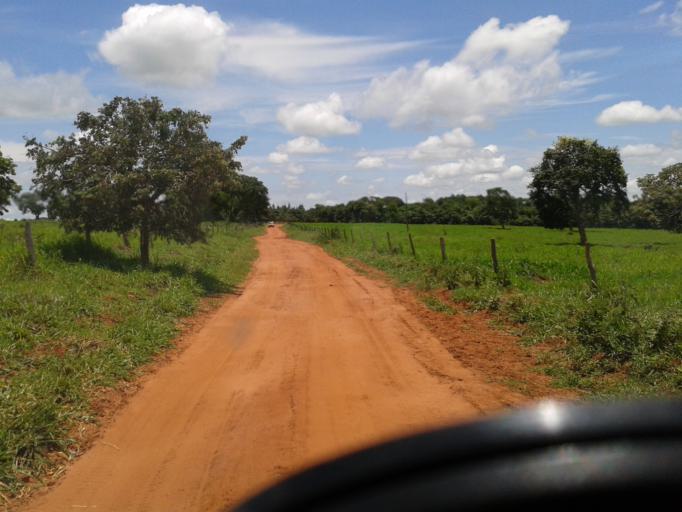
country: BR
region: Minas Gerais
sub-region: Santa Vitoria
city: Santa Vitoria
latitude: -18.9754
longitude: -49.8896
